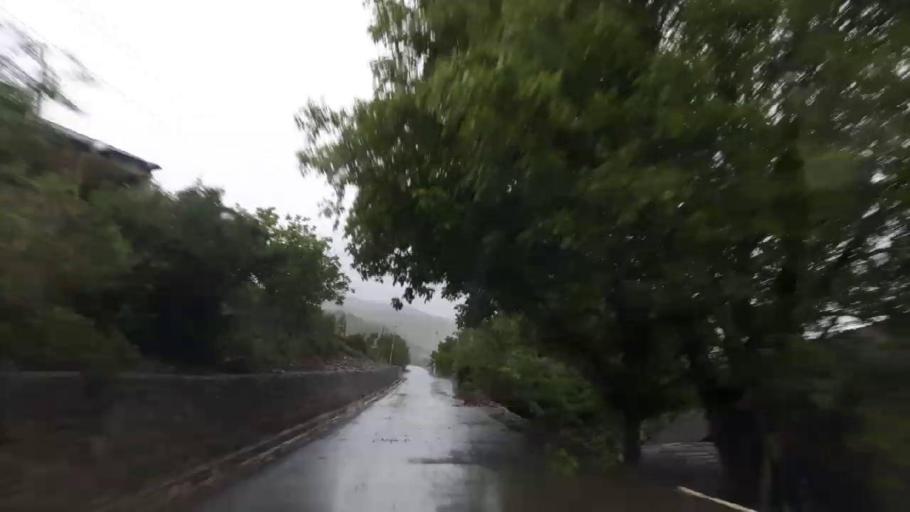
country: GE
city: Agara
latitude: 41.9825
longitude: 43.9333
